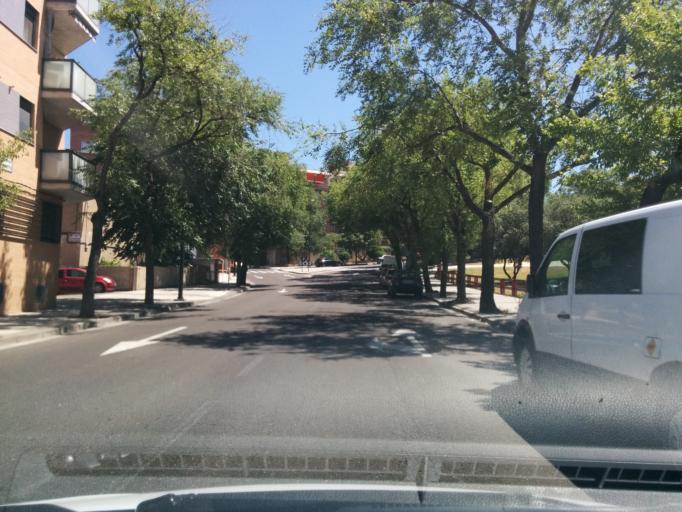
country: ES
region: Aragon
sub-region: Provincia de Zaragoza
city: Zaragoza
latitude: 41.6291
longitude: -0.8782
